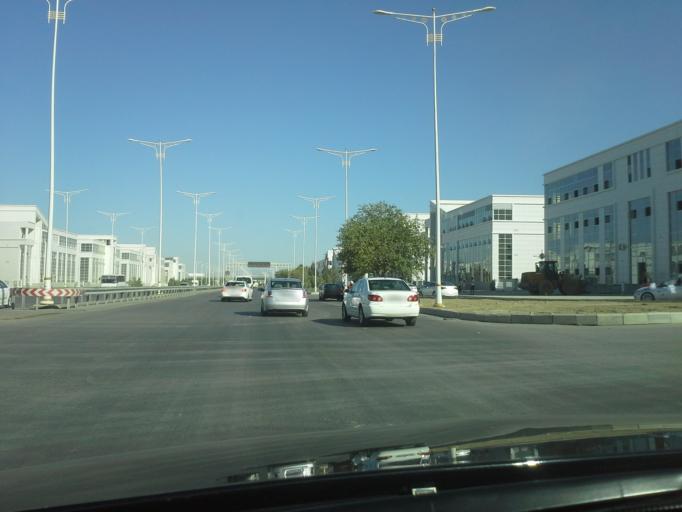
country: TM
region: Ahal
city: Ashgabat
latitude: 37.9654
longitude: 58.4112
